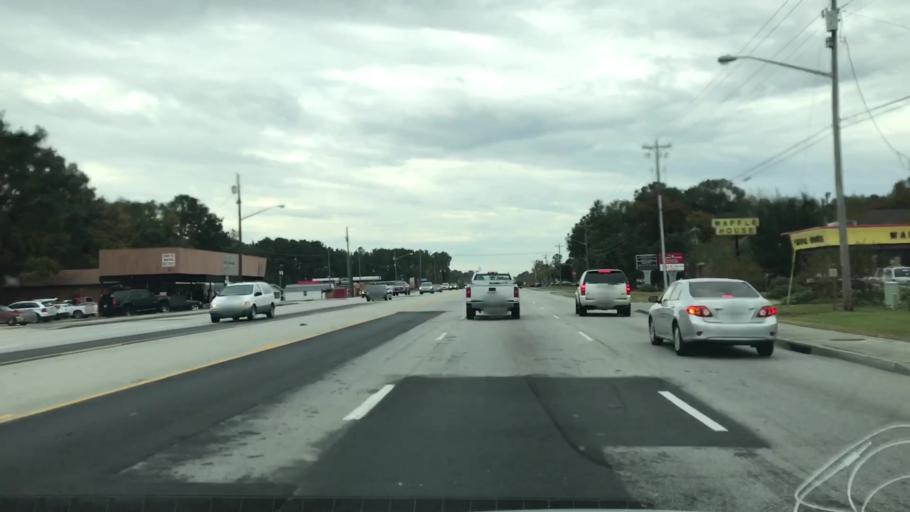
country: US
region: South Carolina
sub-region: Berkeley County
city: Goose Creek
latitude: 32.9912
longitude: -80.0396
